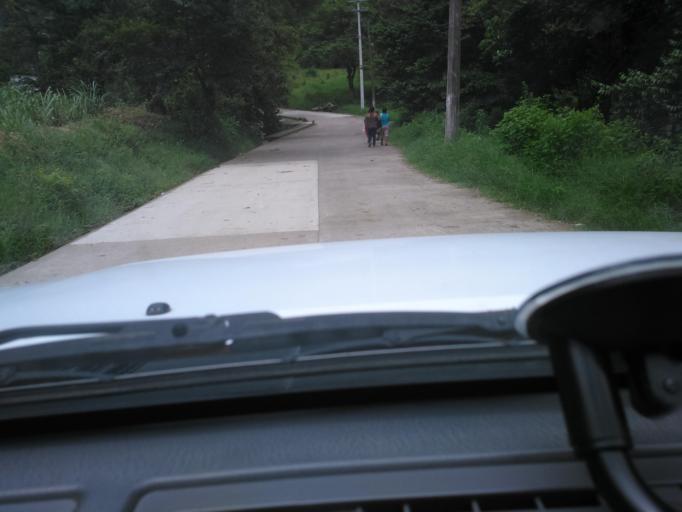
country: MX
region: Veracruz
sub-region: Mariano Escobedo
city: Chicola
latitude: 18.9104
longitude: -97.1095
